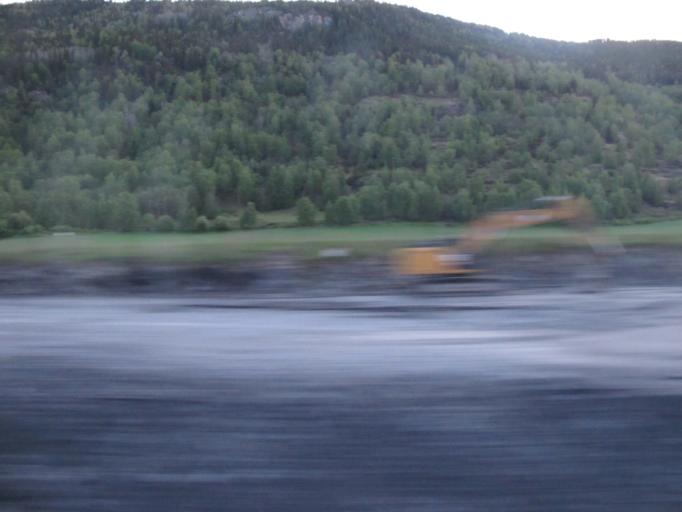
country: NO
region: Oppland
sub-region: Sor-Fron
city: Hundorp
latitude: 61.5480
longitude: 10.0225
